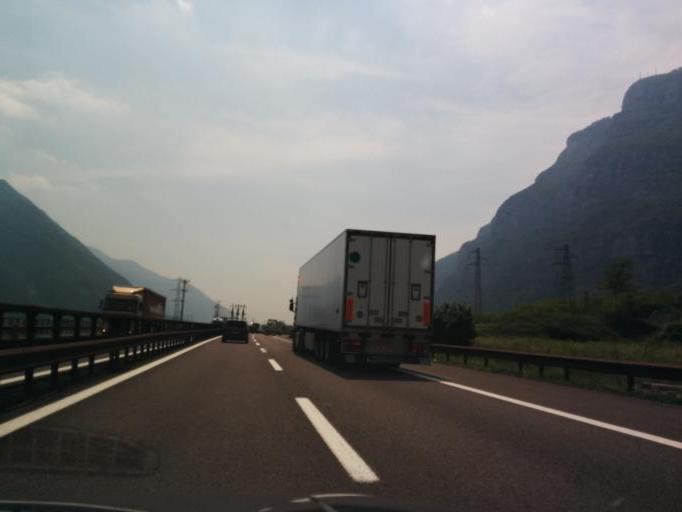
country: IT
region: Veneto
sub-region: Provincia di Verona
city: Rivalta
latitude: 45.6416
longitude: 10.8793
